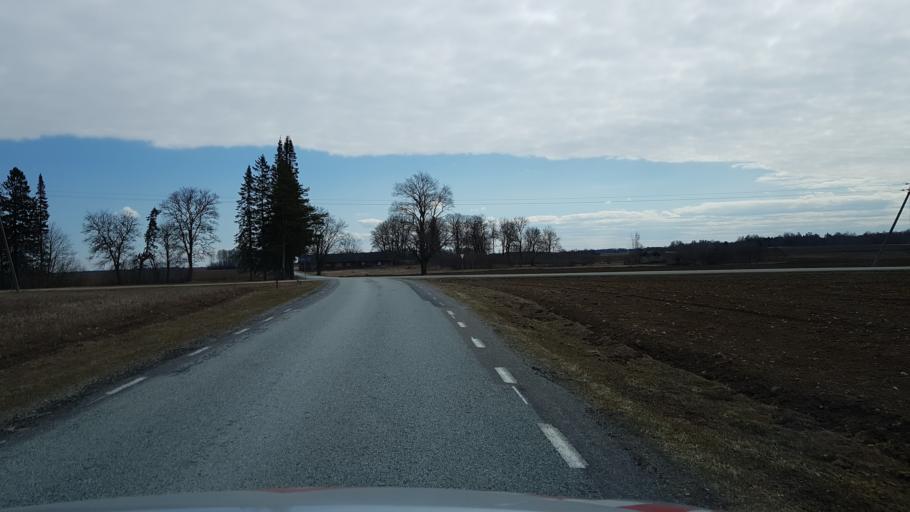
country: EE
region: Laeaene-Virumaa
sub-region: Haljala vald
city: Haljala
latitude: 59.4248
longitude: 26.2248
